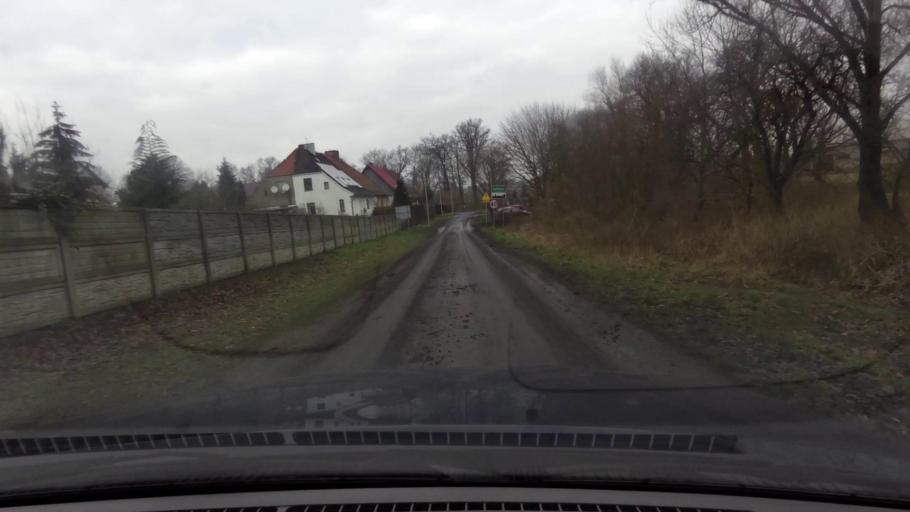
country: PL
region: West Pomeranian Voivodeship
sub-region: Powiat stargardzki
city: Stargard Szczecinski
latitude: 53.3302
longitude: 15.1407
